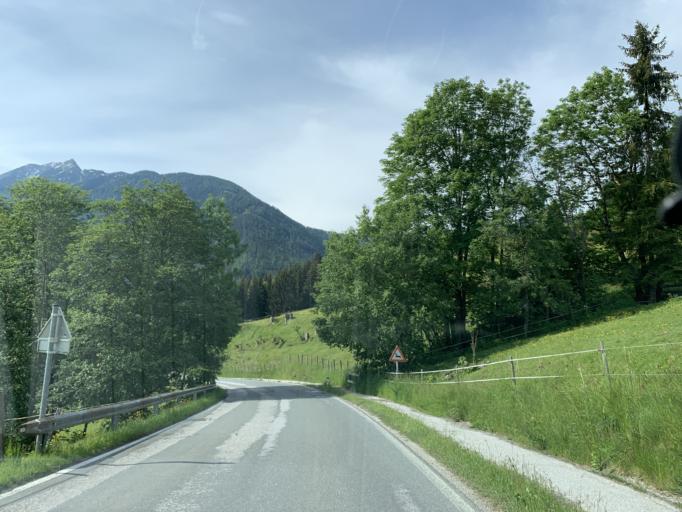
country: AT
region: Styria
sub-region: Politischer Bezirk Liezen
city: Schladming
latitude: 47.3772
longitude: 13.6721
